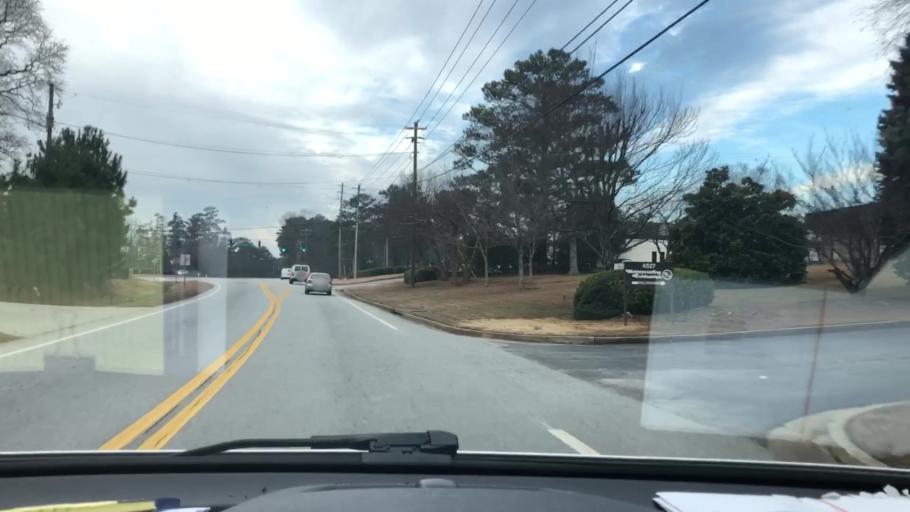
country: US
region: Georgia
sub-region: Gwinnett County
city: Berkeley Lake
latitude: 33.9699
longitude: -84.1801
